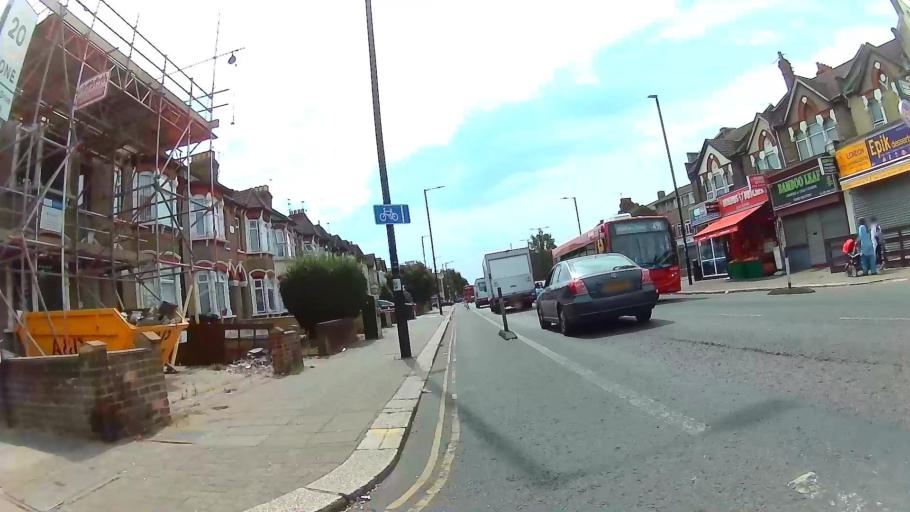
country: GB
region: England
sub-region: Greater London
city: Enfield
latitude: 51.6432
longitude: -0.0467
